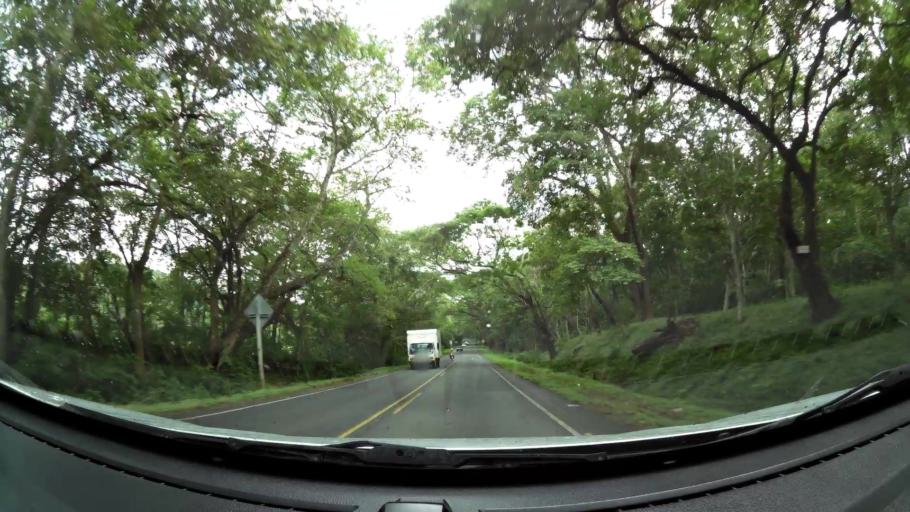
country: CR
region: Guanacaste
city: Juntas
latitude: 10.2414
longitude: -84.9934
